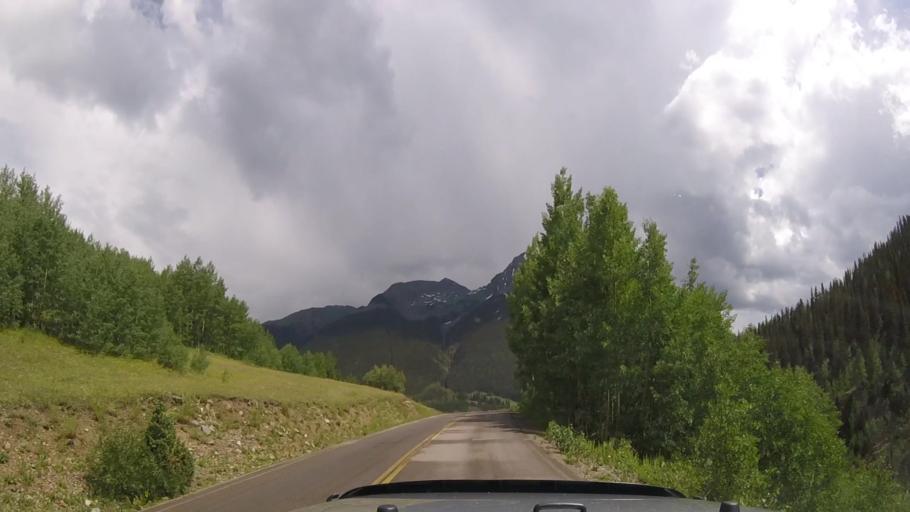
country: US
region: Colorado
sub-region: San Juan County
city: Silverton
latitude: 37.8217
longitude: -107.6638
